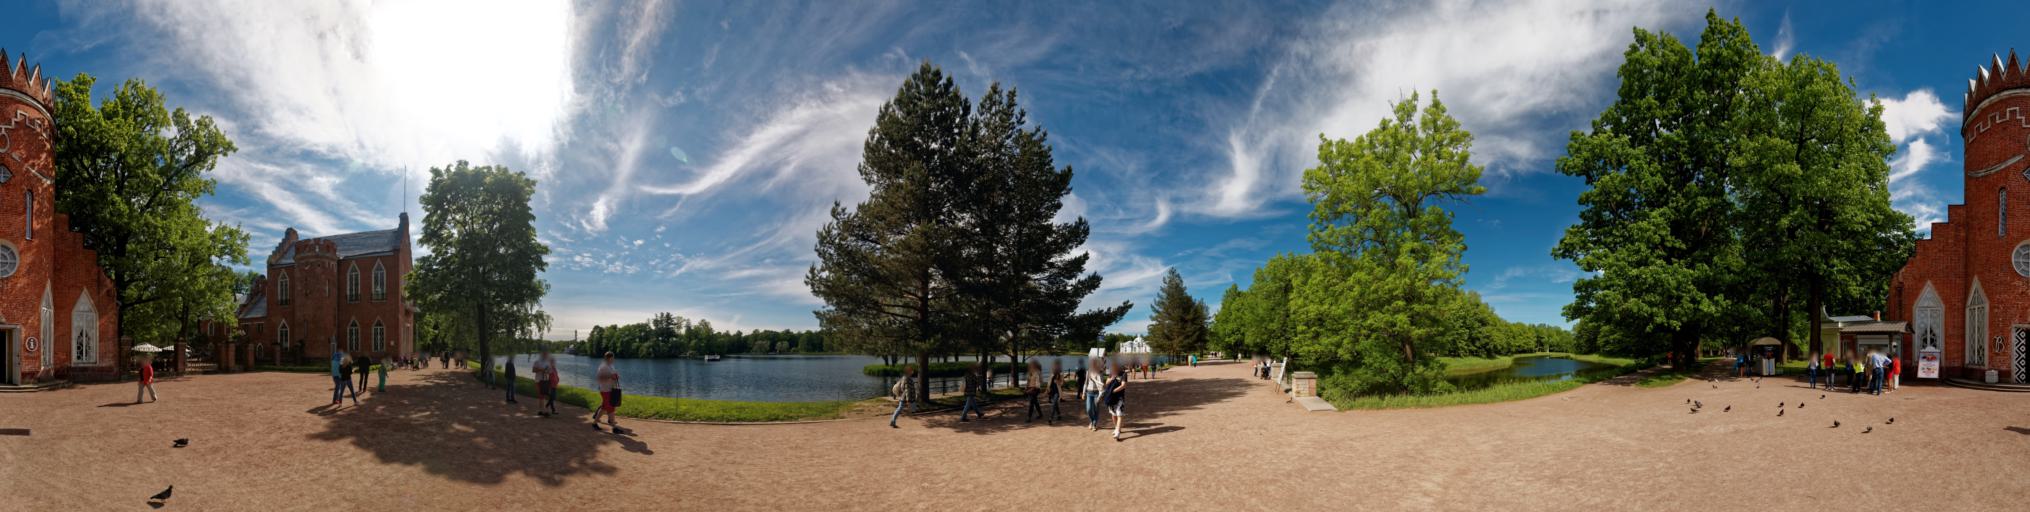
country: RU
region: St.-Petersburg
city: Pushkin
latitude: 59.7109
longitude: 30.3991
